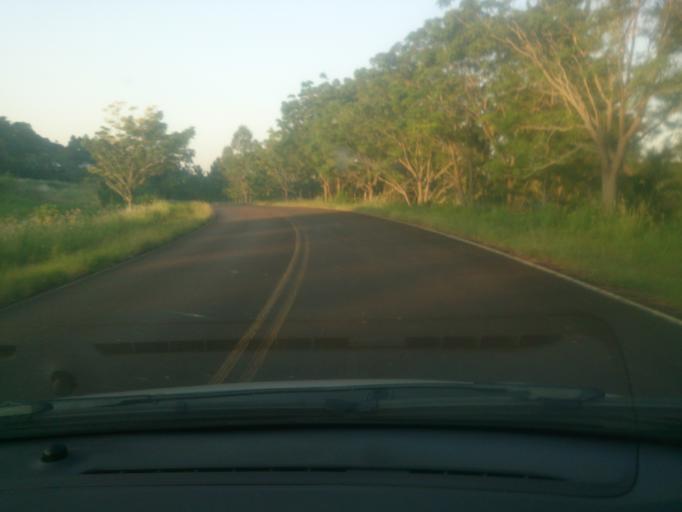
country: AR
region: Misiones
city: Panambi
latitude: -27.6623
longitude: -54.9105
